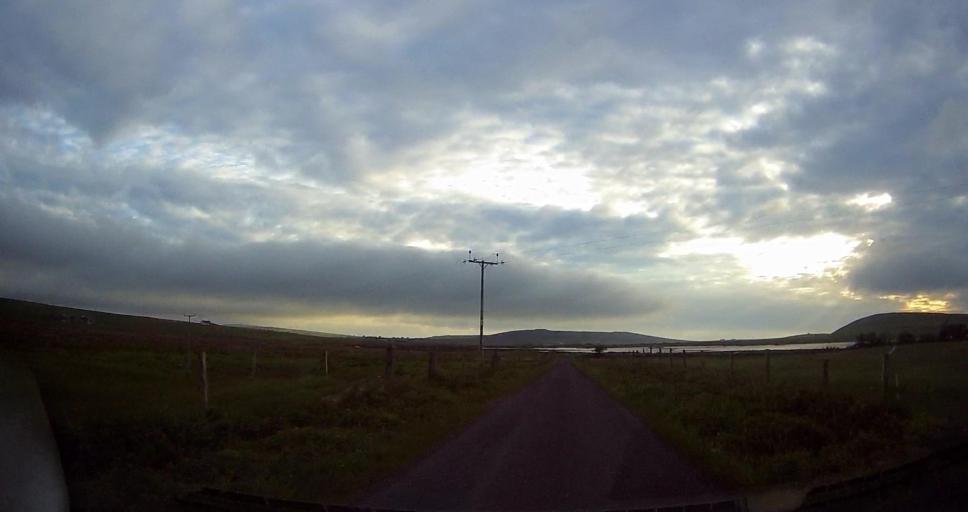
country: GB
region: Scotland
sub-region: Orkney Islands
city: Stromness
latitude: 59.1096
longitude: -3.2261
